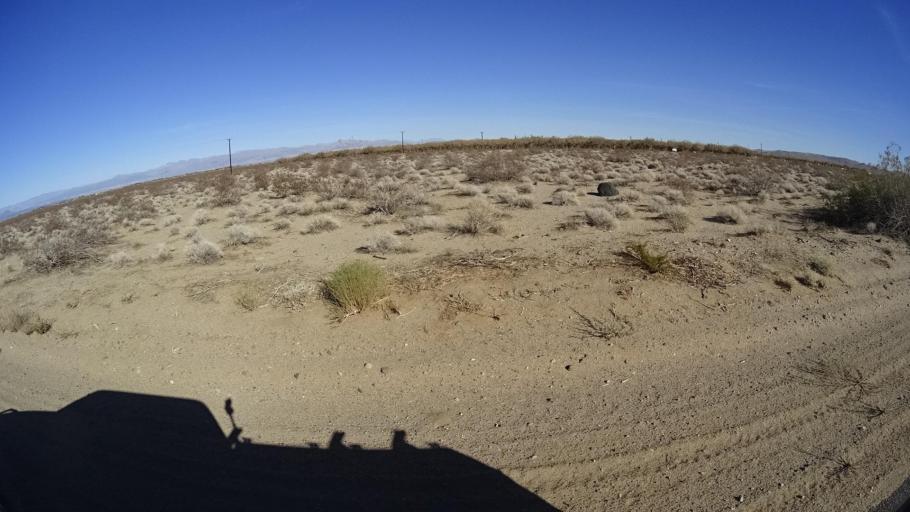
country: US
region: California
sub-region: Kern County
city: China Lake Acres
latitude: 35.5913
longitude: -117.7940
